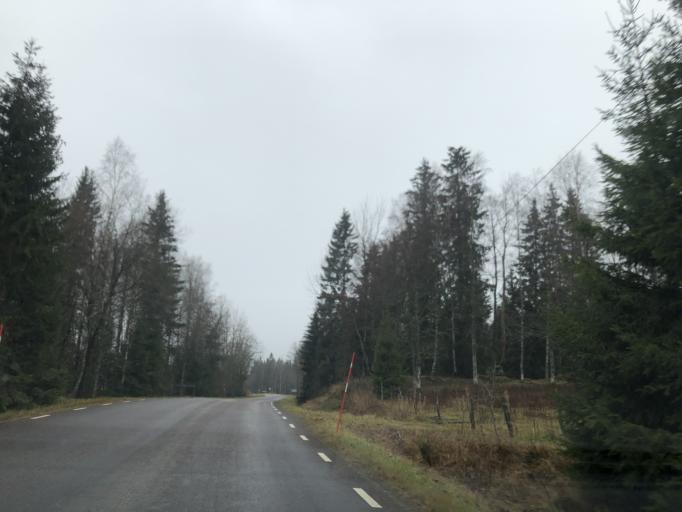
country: SE
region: Vaestra Goetaland
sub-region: Ulricehamns Kommun
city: Ulricehamn
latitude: 57.7530
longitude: 13.5152
